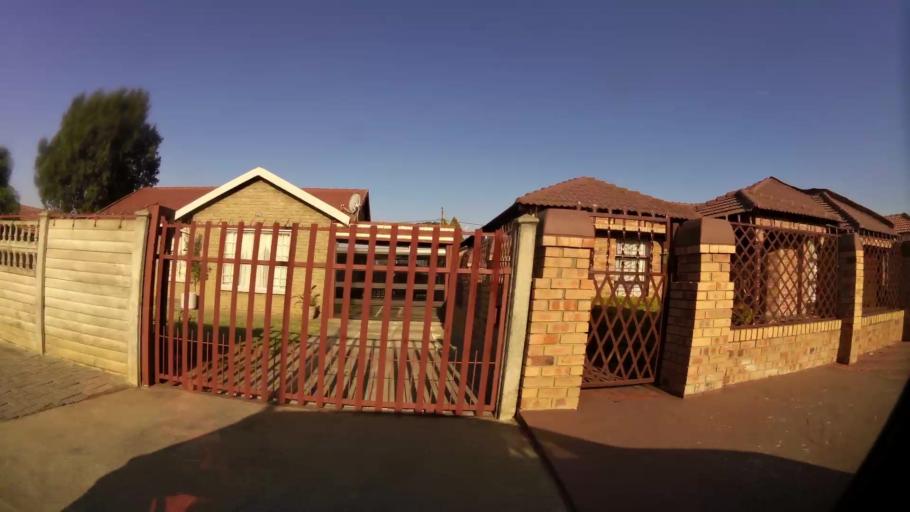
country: ZA
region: North-West
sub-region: Bojanala Platinum District Municipality
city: Rustenburg
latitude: -25.6482
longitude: 27.2208
